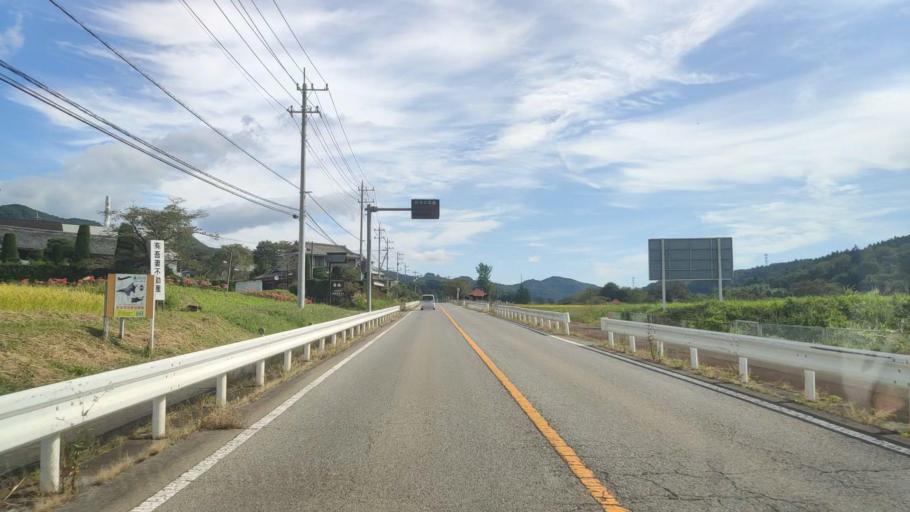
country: JP
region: Gunma
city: Nakanojomachi
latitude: 36.6150
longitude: 138.8901
